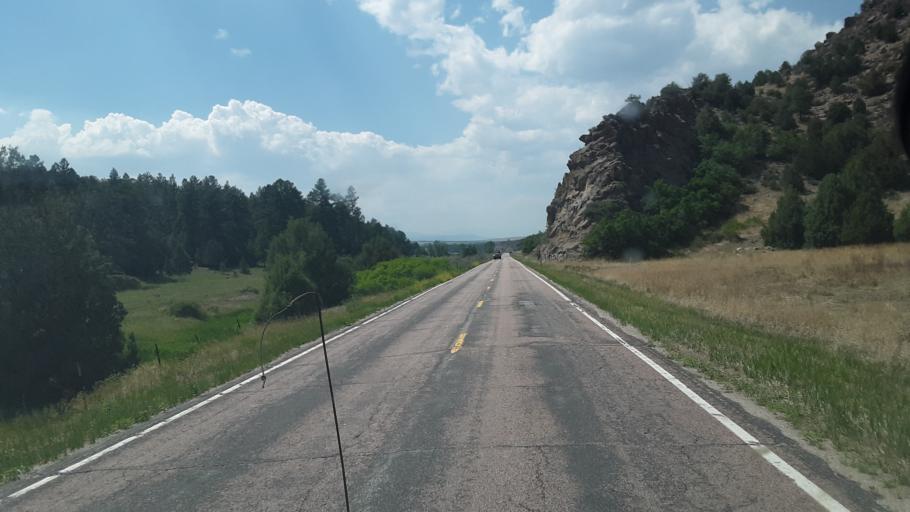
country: US
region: Colorado
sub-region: Custer County
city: Westcliffe
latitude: 38.2529
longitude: -105.5838
